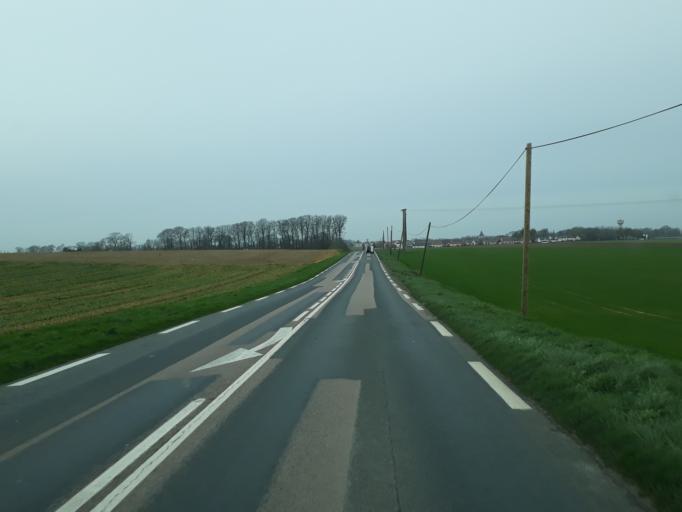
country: FR
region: Haute-Normandie
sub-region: Departement de la Seine-Maritime
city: Breaute
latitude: 49.6168
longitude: 0.4064
